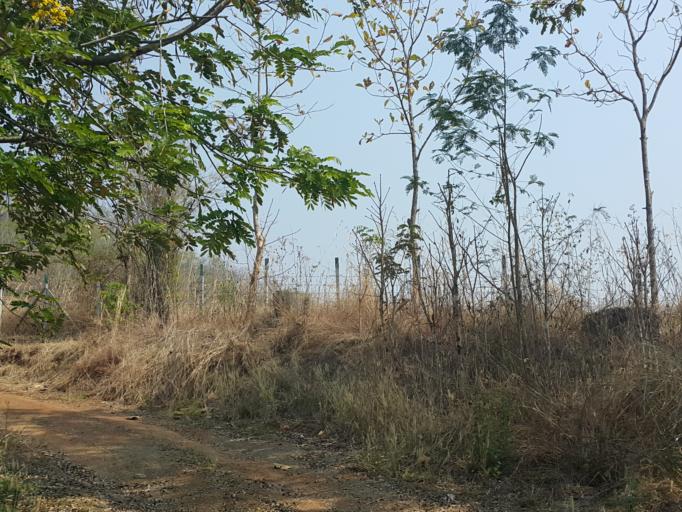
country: TH
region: Chiang Mai
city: Mae On
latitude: 18.7755
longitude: 99.2381
